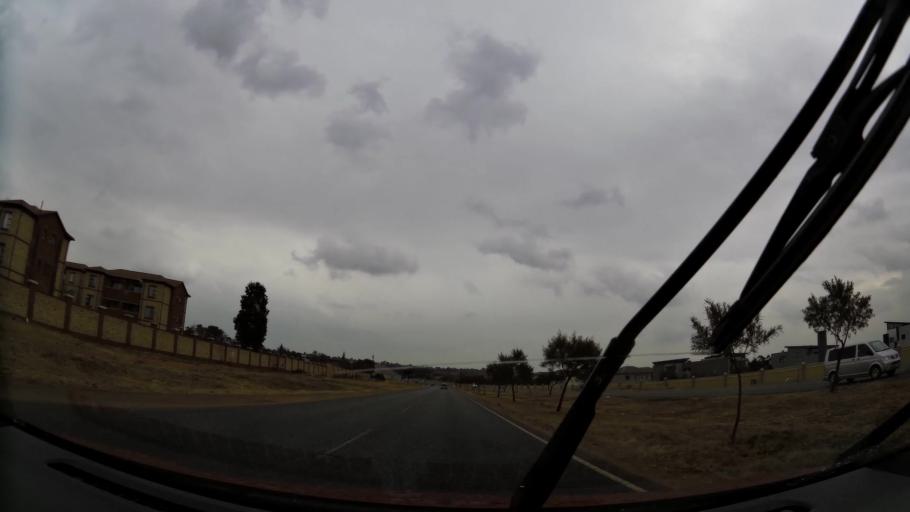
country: ZA
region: Gauteng
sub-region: City of Johannesburg Metropolitan Municipality
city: Roodepoort
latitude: -26.0910
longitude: 27.9275
